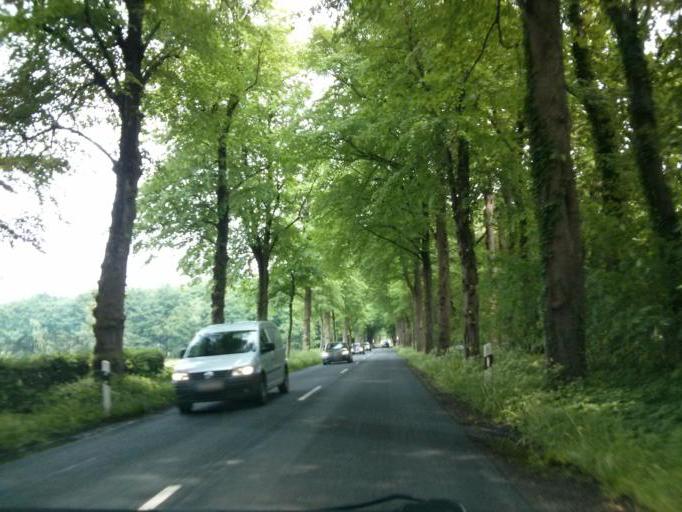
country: DE
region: Lower Saxony
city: Loxstedt
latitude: 53.4801
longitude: 8.6761
